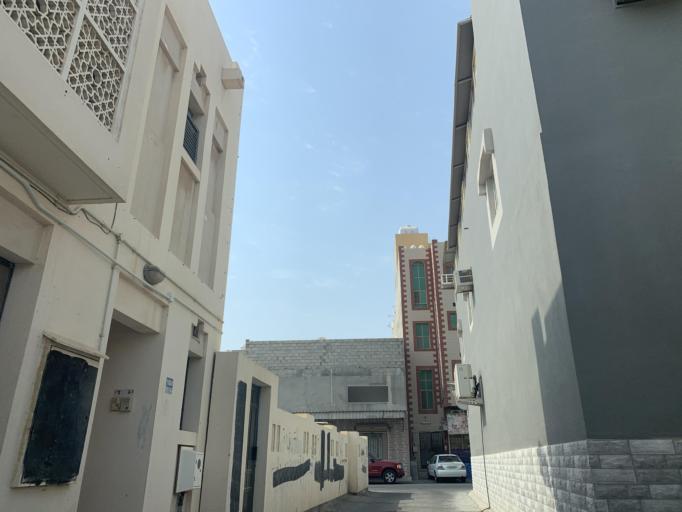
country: BH
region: Manama
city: Jidd Hafs
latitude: 26.2107
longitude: 50.4877
